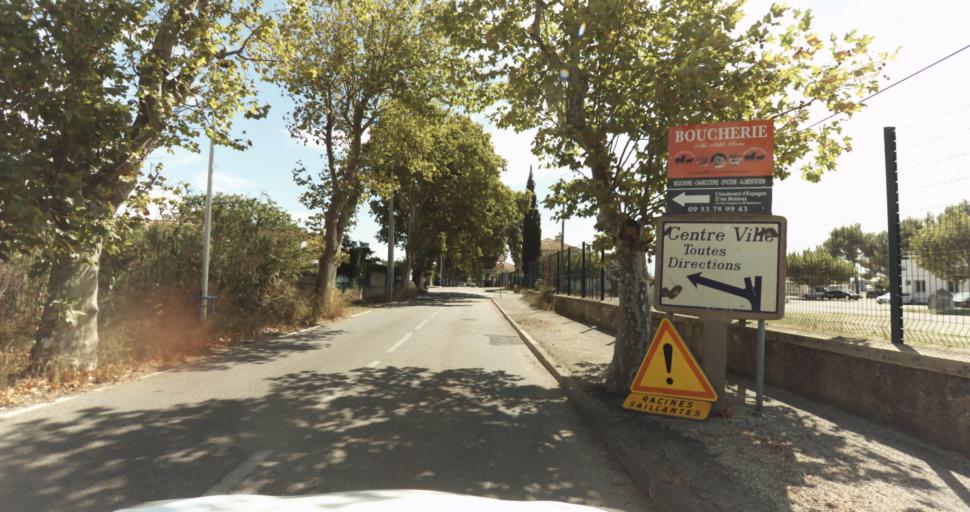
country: FR
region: Provence-Alpes-Cote d'Azur
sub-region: Departement des Bouches-du-Rhone
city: Miramas
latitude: 43.5834
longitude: 4.9941
